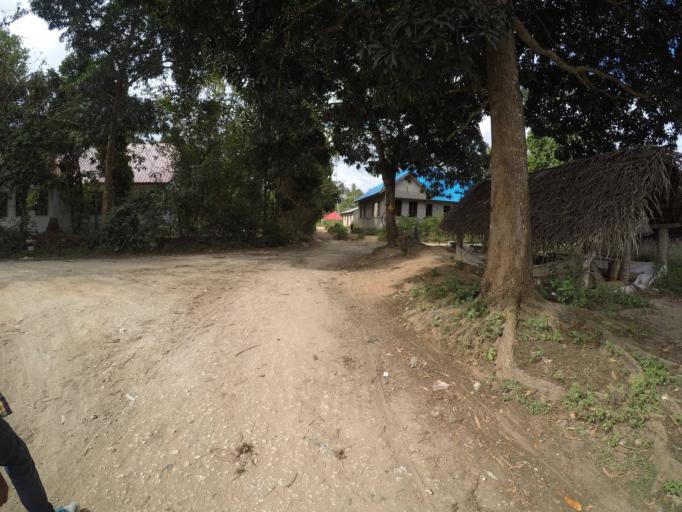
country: TZ
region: Zanzibar Central/South
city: Koani
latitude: -6.1893
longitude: 39.2643
